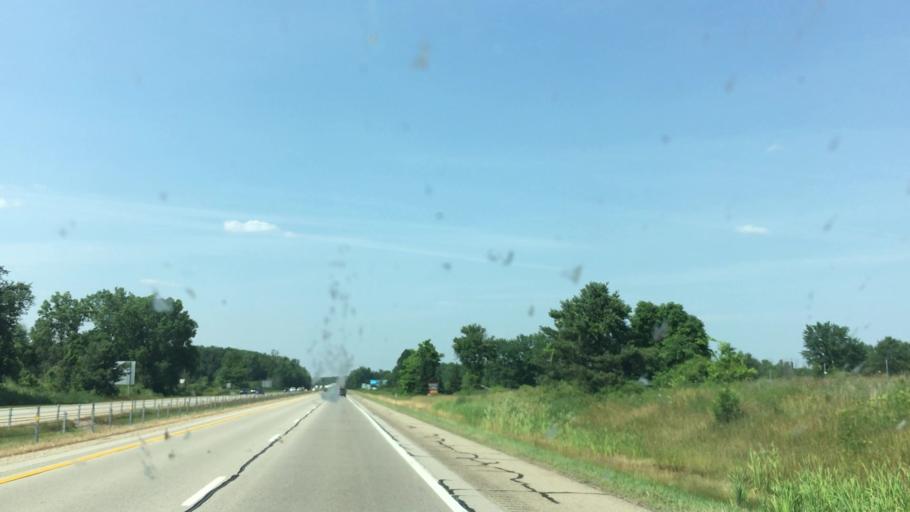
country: US
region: Michigan
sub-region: Allegan County
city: Wayland
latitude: 42.6936
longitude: -85.6599
